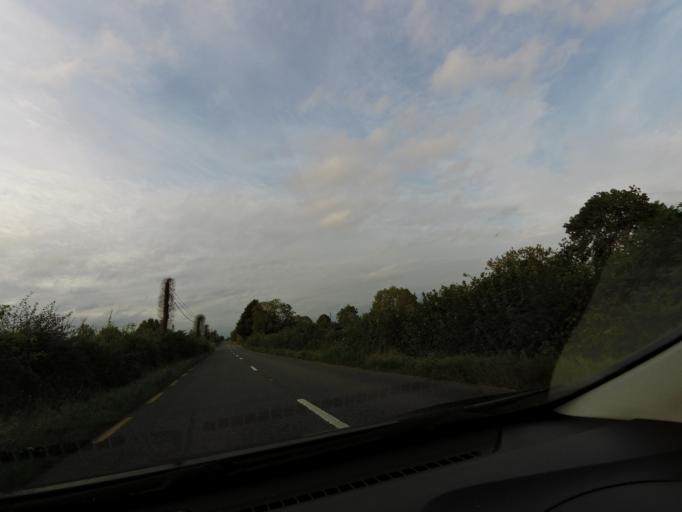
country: IE
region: Leinster
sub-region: Uibh Fhaili
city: Ferbane
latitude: 53.3180
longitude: -7.8213
